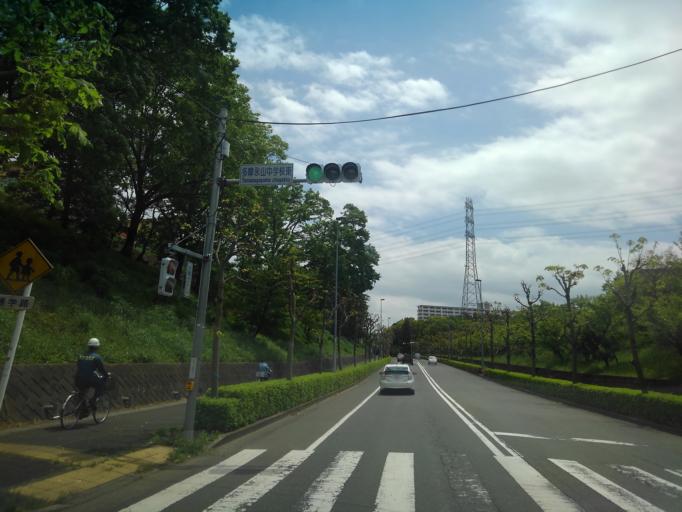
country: JP
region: Tokyo
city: Hino
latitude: 35.6248
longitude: 139.4498
